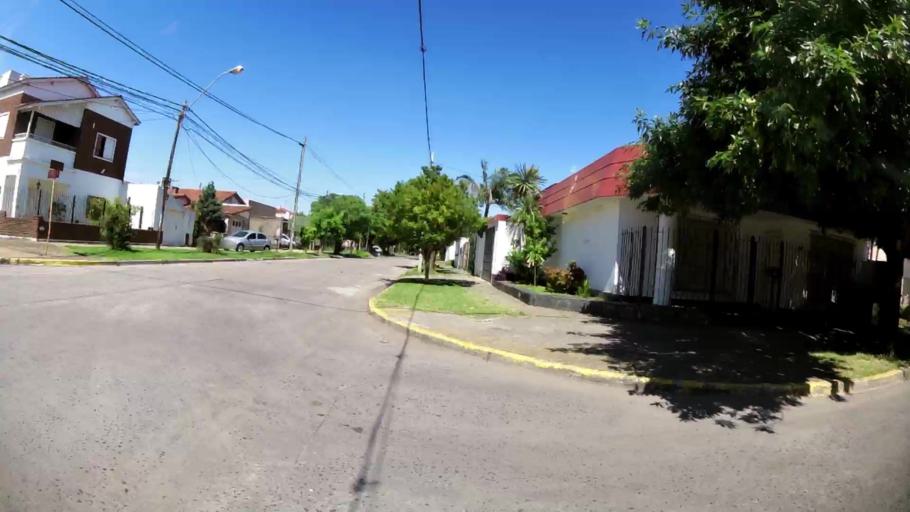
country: AR
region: Buenos Aires
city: Ituzaingo
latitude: -34.6627
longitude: -58.6627
